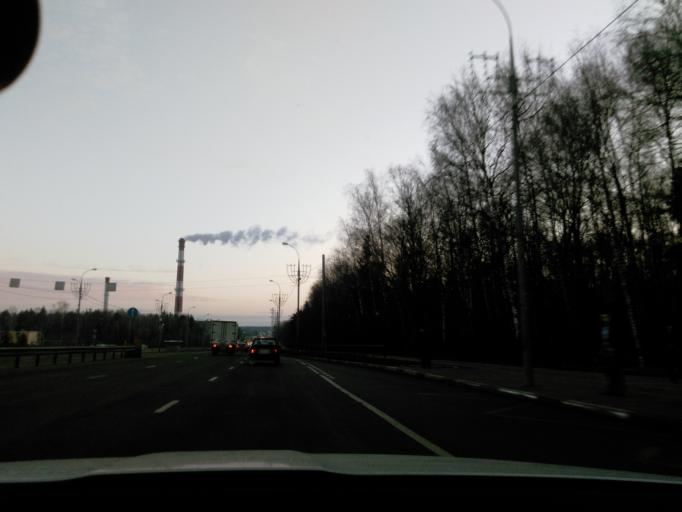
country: RU
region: Moscow
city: Zelenograd
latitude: 55.9999
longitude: 37.1939
